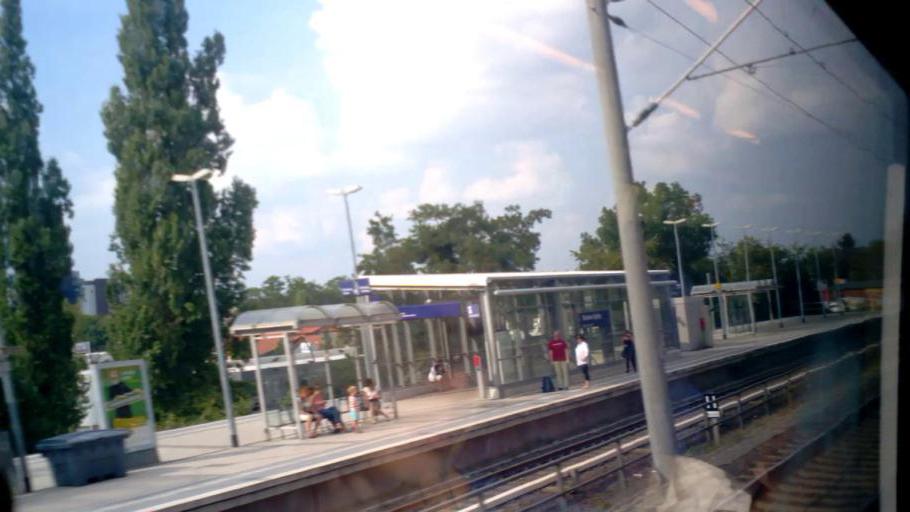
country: DE
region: Berlin
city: Lichterfelde
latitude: 52.4189
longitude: 13.3145
